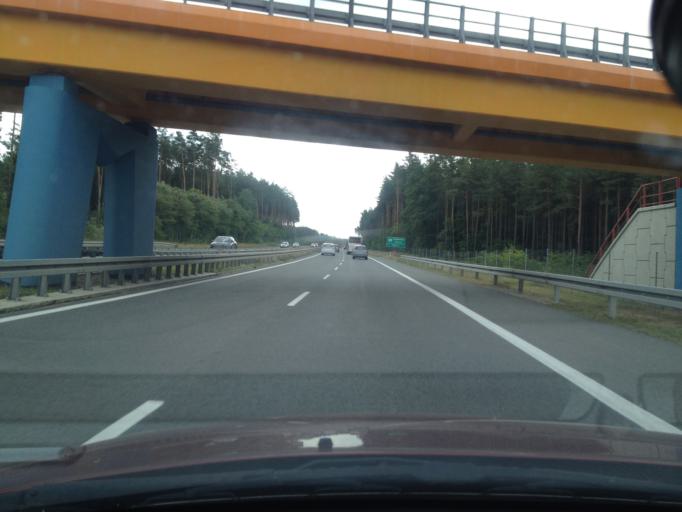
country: PL
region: West Pomeranian Voivodeship
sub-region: Powiat goleniowski
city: Goleniow
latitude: 53.6123
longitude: 14.8182
